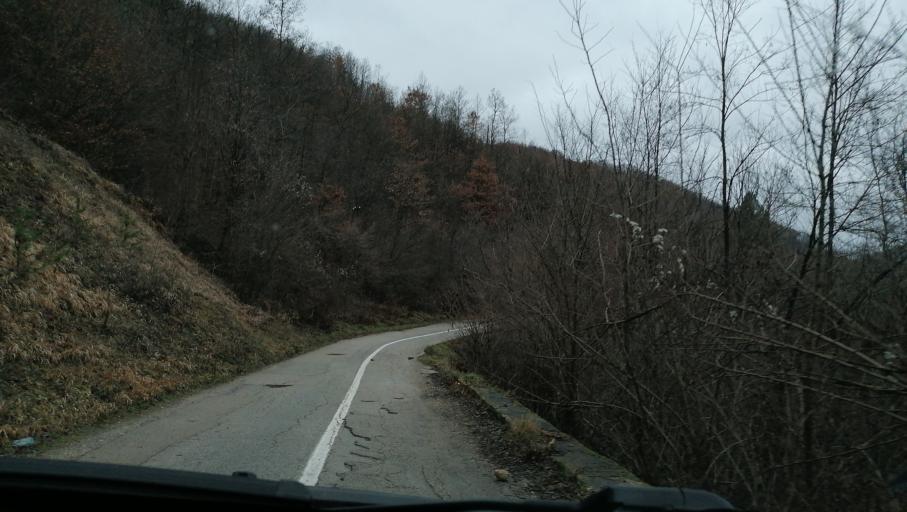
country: RS
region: Central Serbia
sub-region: Pirotski Okrug
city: Dimitrovgrad
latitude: 42.9762
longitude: 22.7847
